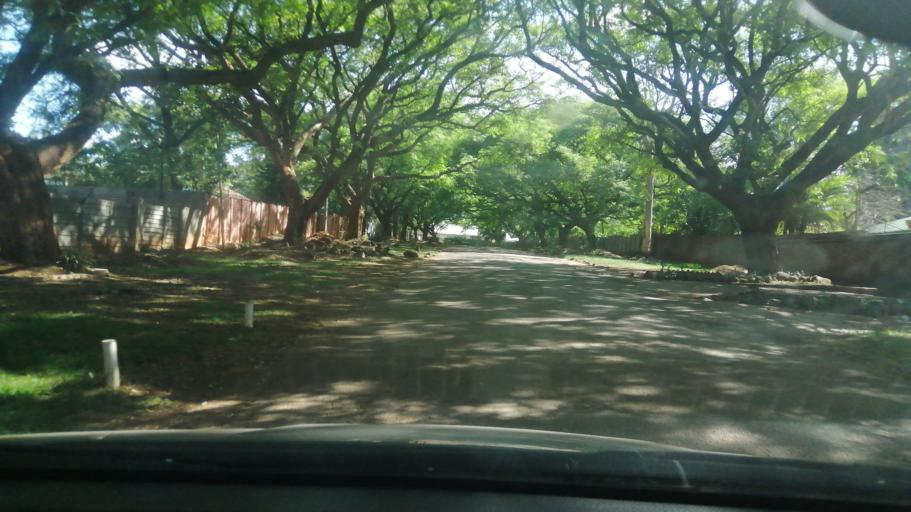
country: ZW
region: Harare
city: Harare
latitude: -17.7925
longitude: 31.0584
